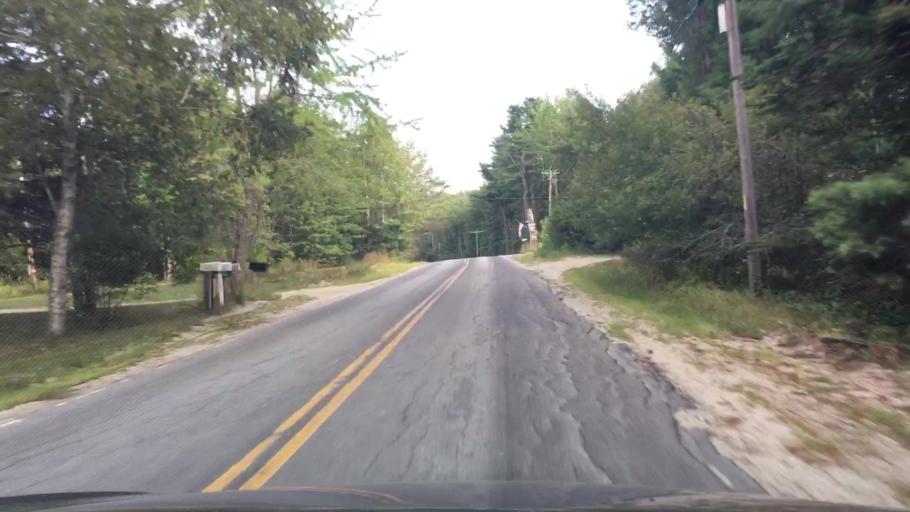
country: US
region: Maine
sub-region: Hancock County
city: Surry
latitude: 44.5069
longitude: -68.5948
